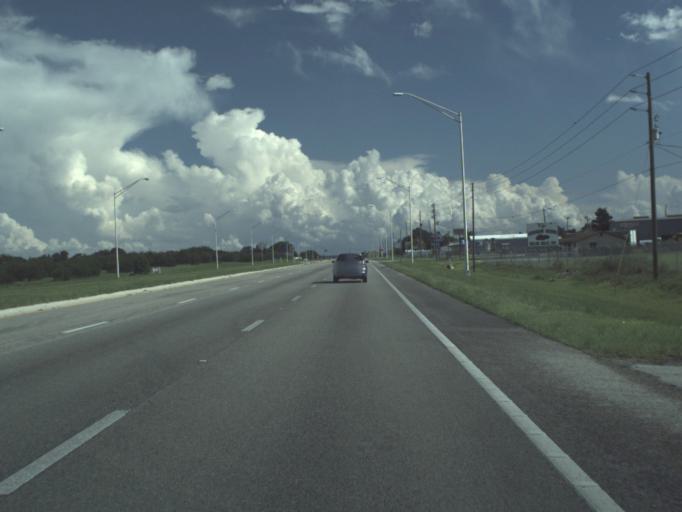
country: US
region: Florida
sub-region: Highlands County
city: Avon Park
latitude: 27.6417
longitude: -81.5257
